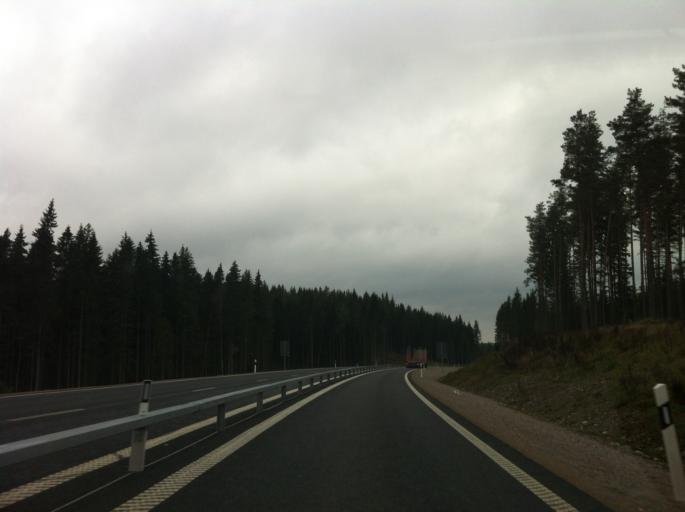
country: SE
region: Joenkoeping
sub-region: Vetlanda Kommun
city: Vetlanda
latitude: 57.4233
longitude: 15.1894
